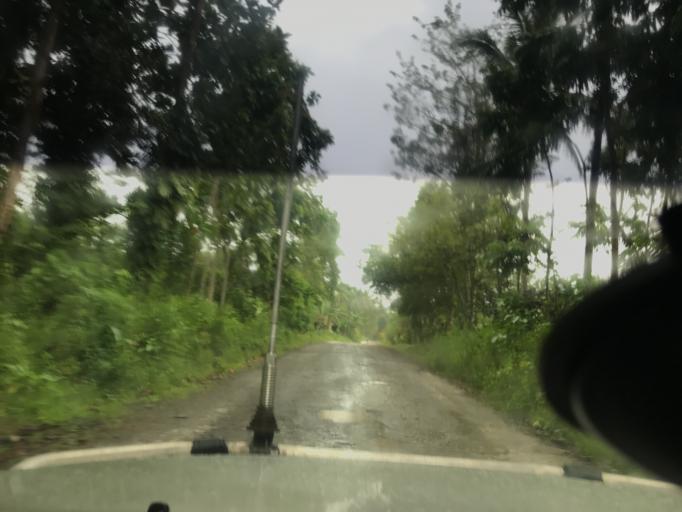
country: SB
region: Malaita
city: Auki
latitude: -8.9932
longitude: 160.7876
